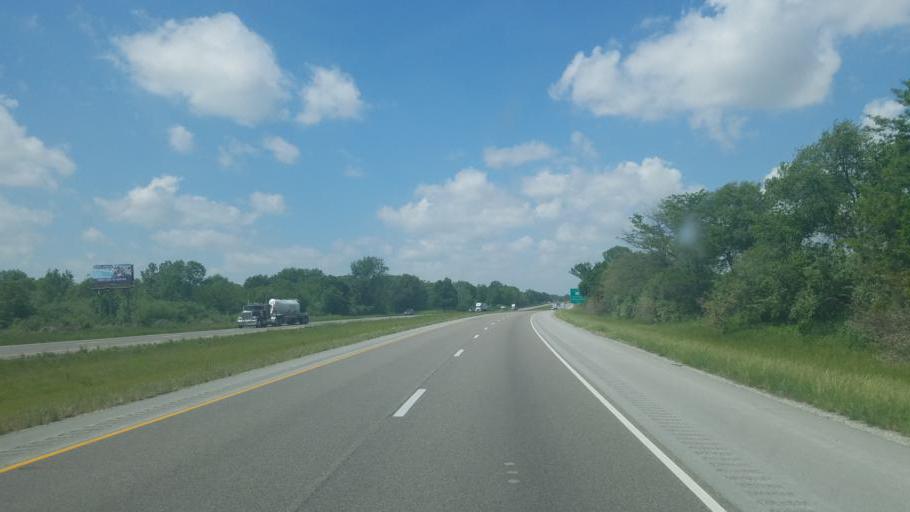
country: US
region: Illinois
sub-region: Cumberland County
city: Greenup
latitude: 39.2605
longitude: -88.1297
